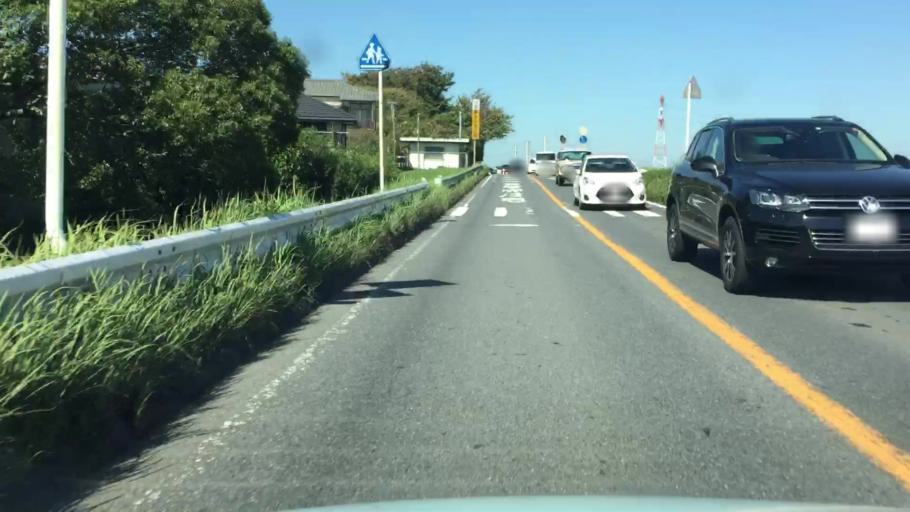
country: JP
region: Ibaraki
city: Fujishiro
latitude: 35.8557
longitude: 140.1355
